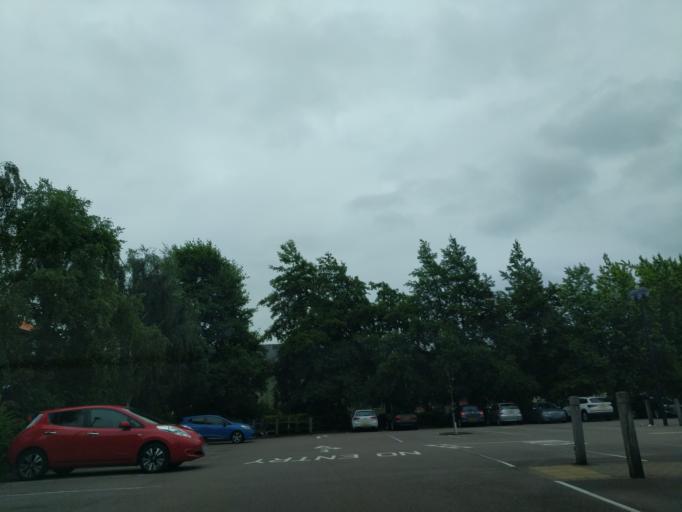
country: GB
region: England
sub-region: Nottinghamshire
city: Newark on Trent
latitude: 53.0812
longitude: -0.8118
